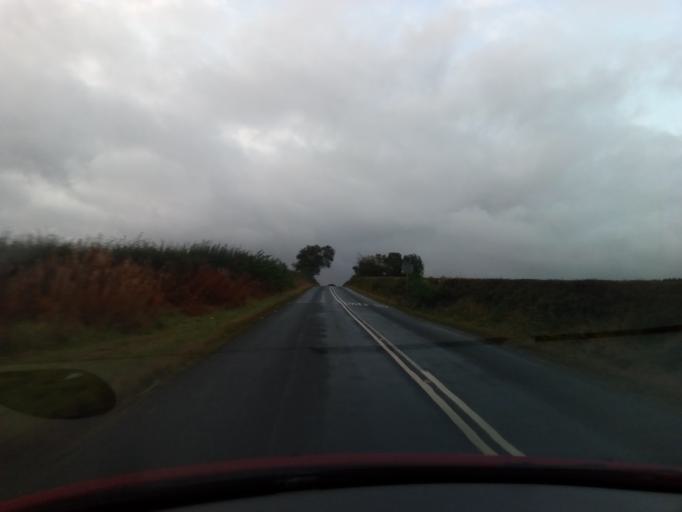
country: GB
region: England
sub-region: Darlington
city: Summerhouse
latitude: 54.5981
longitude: -1.6807
